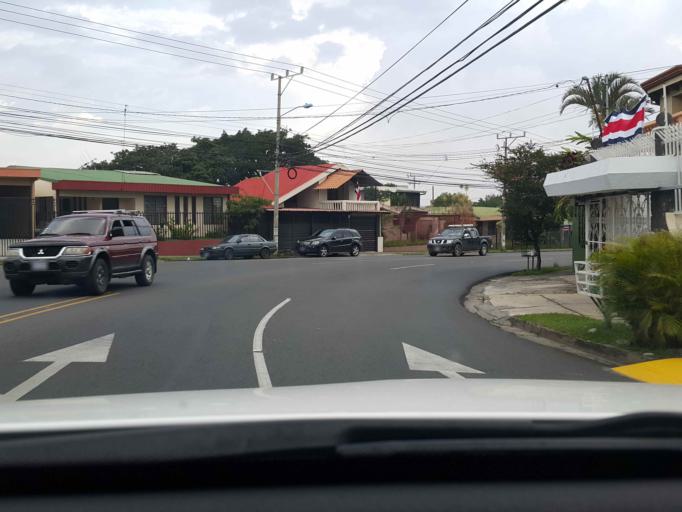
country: CR
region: Heredia
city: Heredia
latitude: 9.9972
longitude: -84.1089
